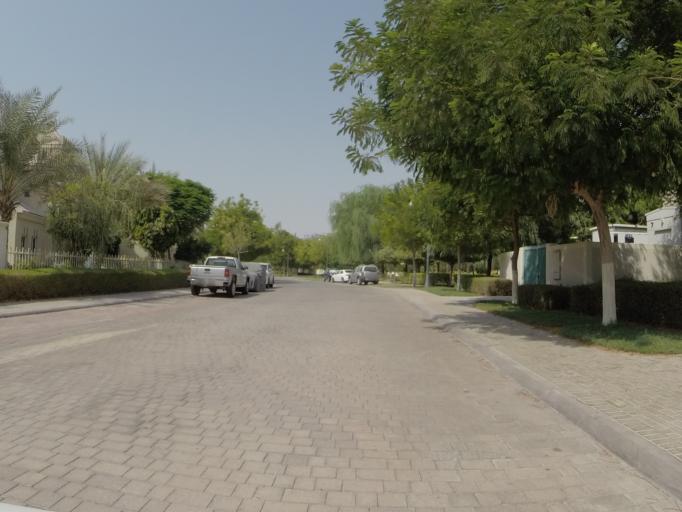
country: AE
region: Dubai
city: Dubai
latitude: 25.0341
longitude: 55.2141
